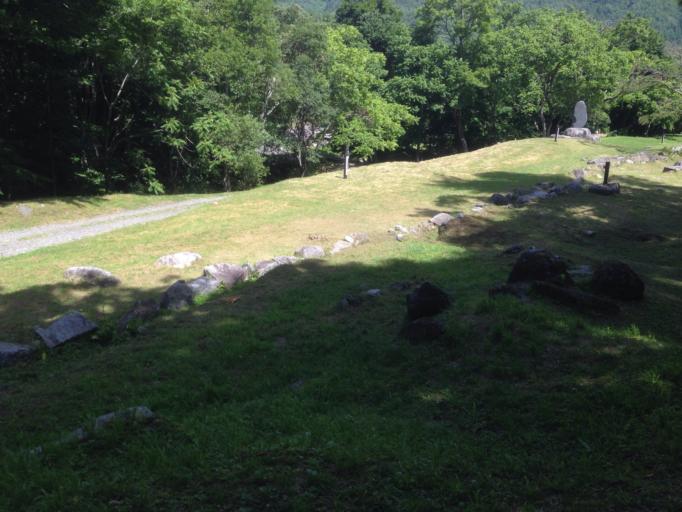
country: JP
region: Iwate
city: Tono
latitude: 39.3433
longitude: 141.6825
